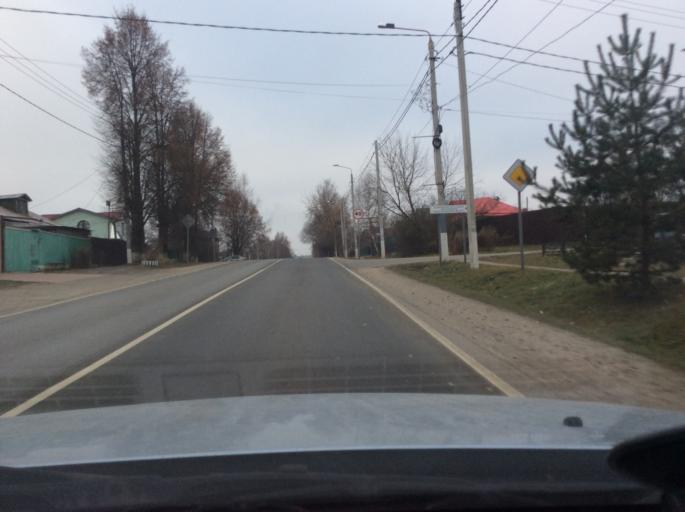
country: RU
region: Moskovskaya
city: Filimonki
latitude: 55.5222
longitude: 37.3753
